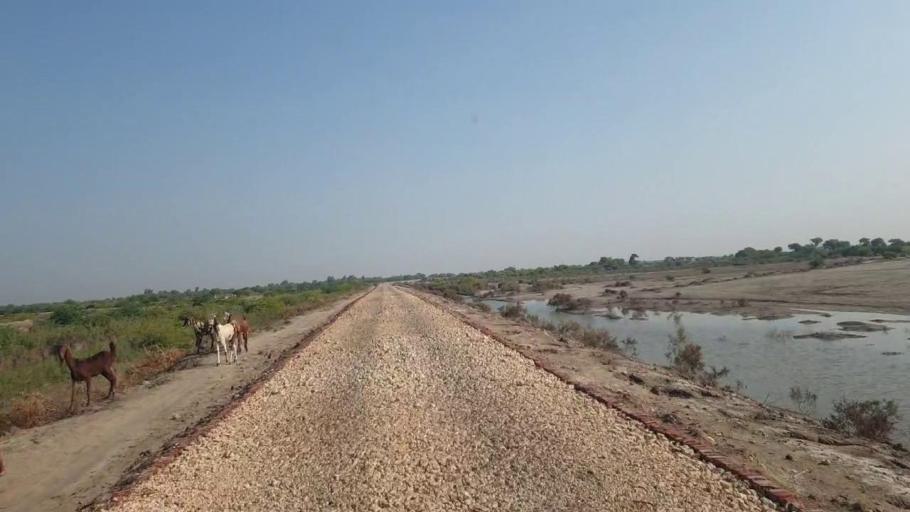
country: PK
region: Sindh
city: Badin
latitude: 24.4882
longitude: 68.7489
